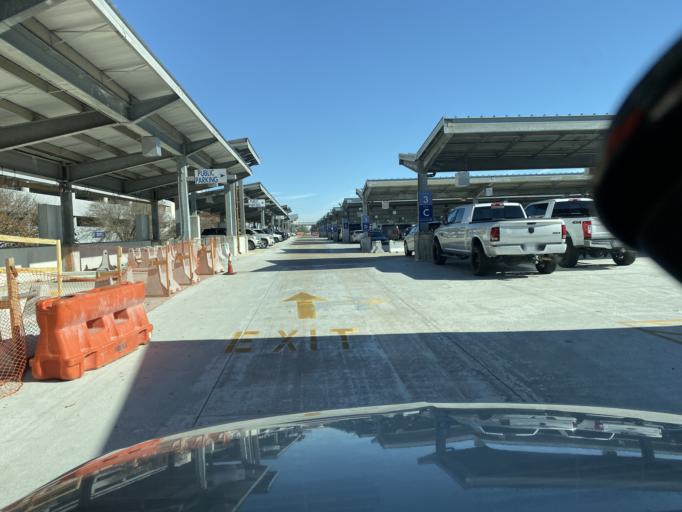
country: US
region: Texas
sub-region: Travis County
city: Hornsby Bend
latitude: 30.2040
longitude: -97.6683
